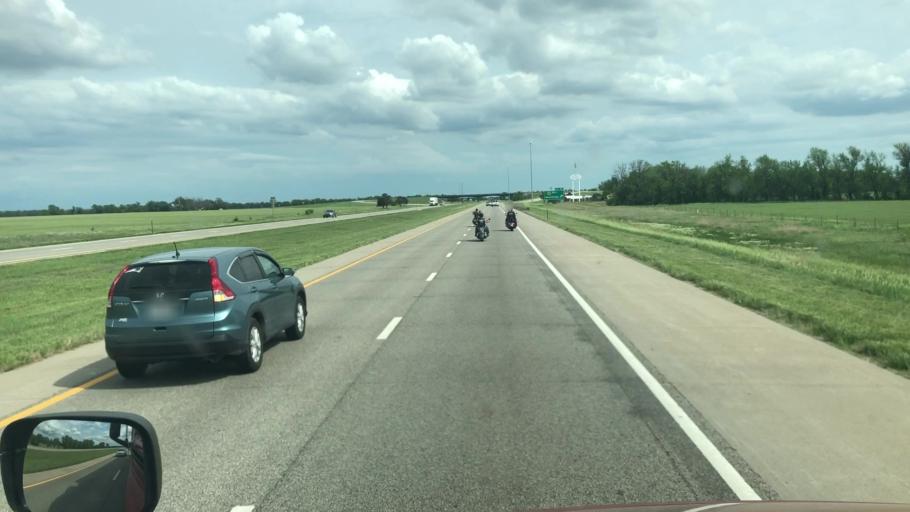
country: US
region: Kansas
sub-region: McPherson County
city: Moundridge
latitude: 38.2084
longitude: -97.4931
